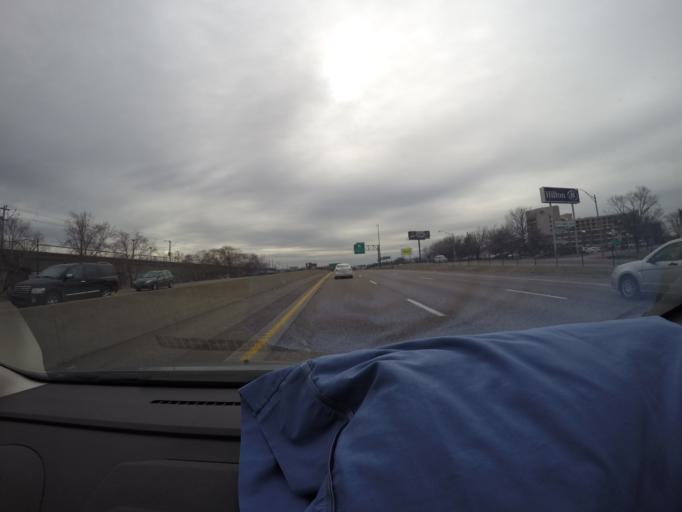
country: US
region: Missouri
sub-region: Saint Louis County
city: Woodson Terrace
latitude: 38.7378
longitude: -90.3604
